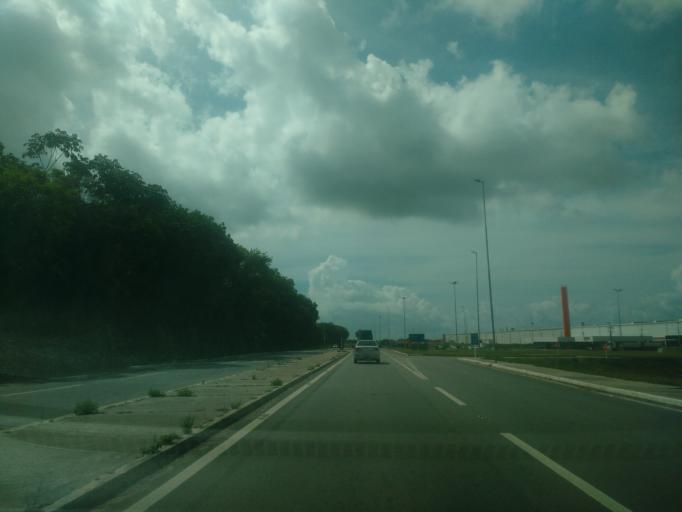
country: BR
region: Alagoas
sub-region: Marechal Deodoro
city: Marechal Deodoro
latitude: -9.6837
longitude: -35.8280
